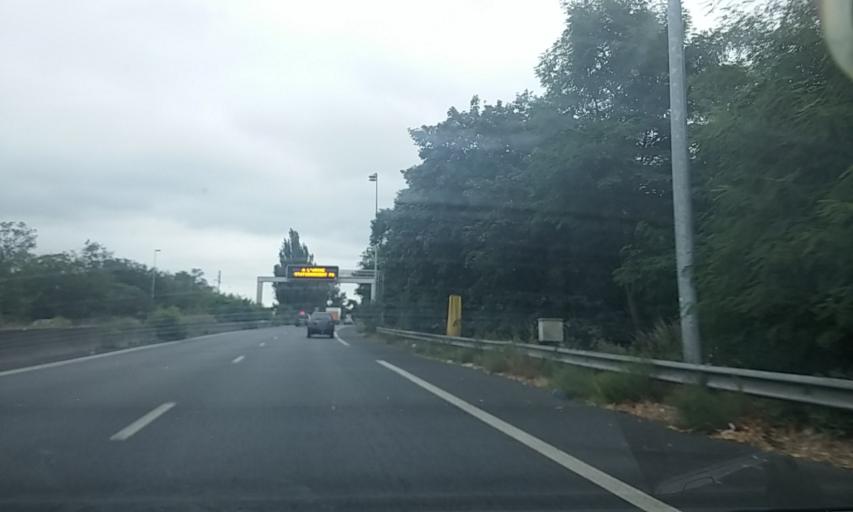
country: FR
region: Ile-de-France
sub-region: Departement du Val-de-Marne
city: Rungis
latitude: 48.7458
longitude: 2.3601
